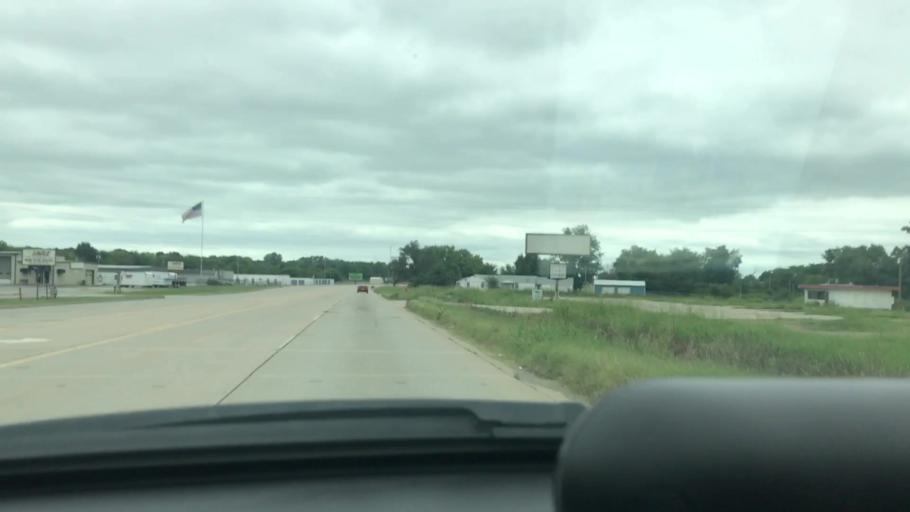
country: US
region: Oklahoma
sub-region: Mayes County
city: Chouteau
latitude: 36.1772
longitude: -95.3424
